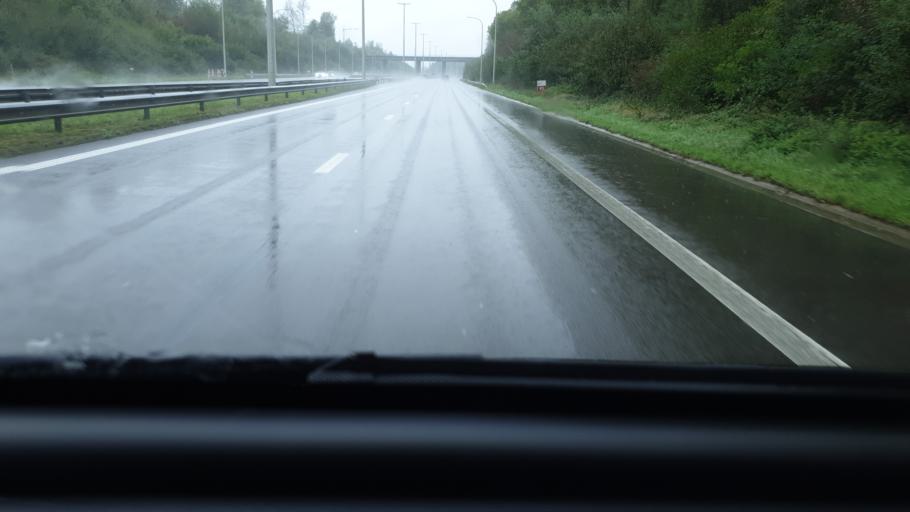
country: BE
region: Wallonia
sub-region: Province du Hainaut
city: Farciennes
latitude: 50.4620
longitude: 4.5013
